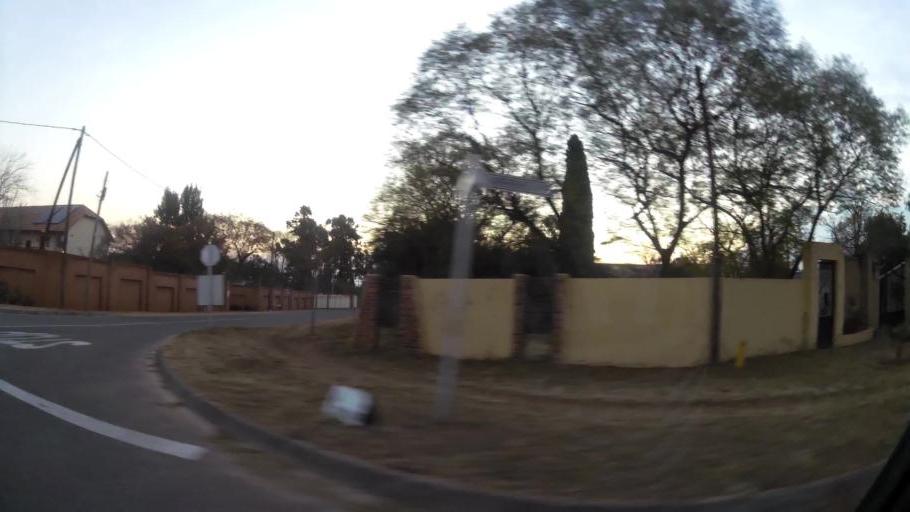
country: ZA
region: Gauteng
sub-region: City of Johannesburg Metropolitan Municipality
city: Diepsloot
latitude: -25.9680
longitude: 28.0653
